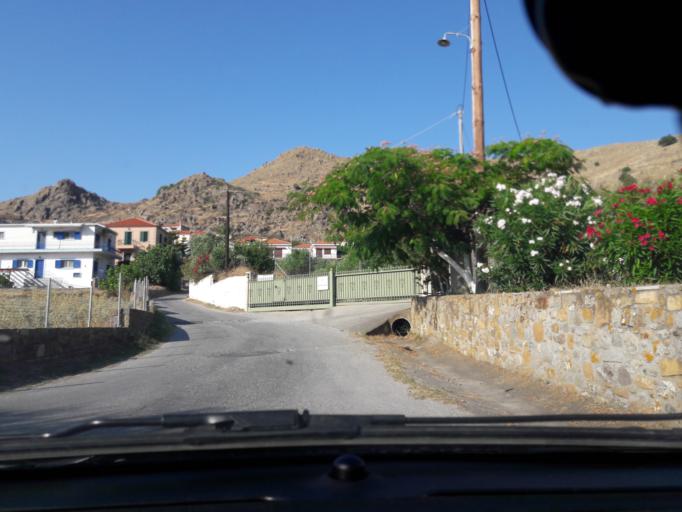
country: GR
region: North Aegean
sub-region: Nomos Lesvou
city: Myrina
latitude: 39.8520
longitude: 25.0876
